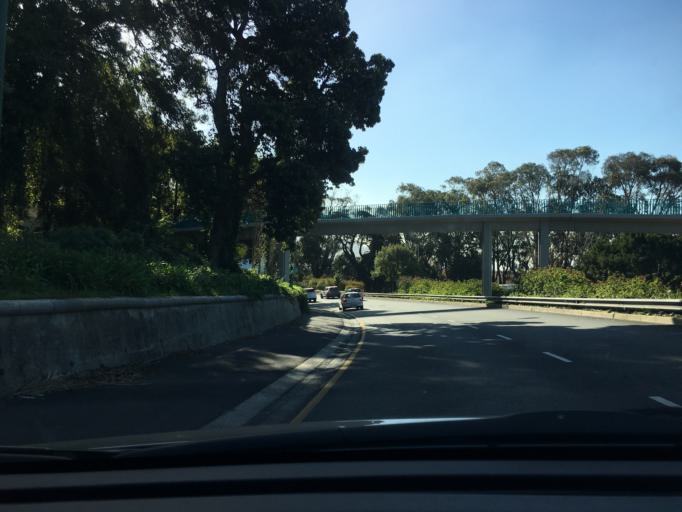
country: ZA
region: Western Cape
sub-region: City of Cape Town
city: Claremont
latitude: -33.9940
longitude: 18.4554
